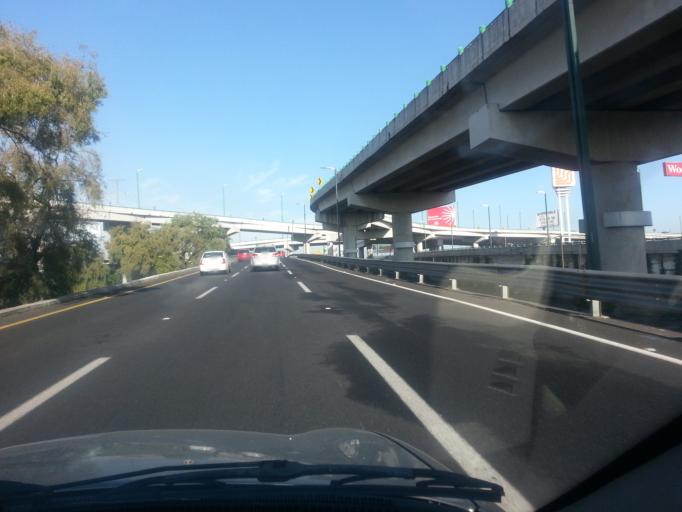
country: MX
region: Mexico
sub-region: San Mateo Atenco
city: Santa Maria la Asuncion
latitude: 19.2864
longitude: -99.5540
